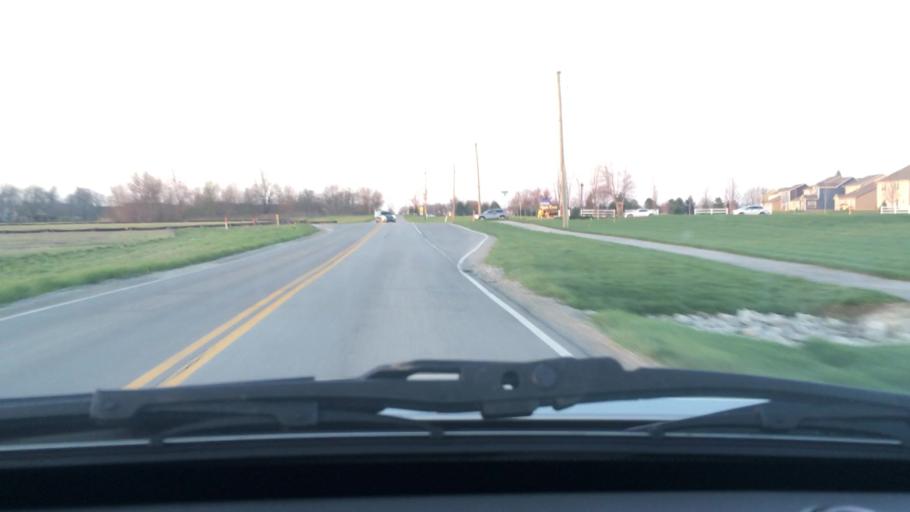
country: US
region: Indiana
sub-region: Hamilton County
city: Westfield
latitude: 40.0390
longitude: -86.1650
